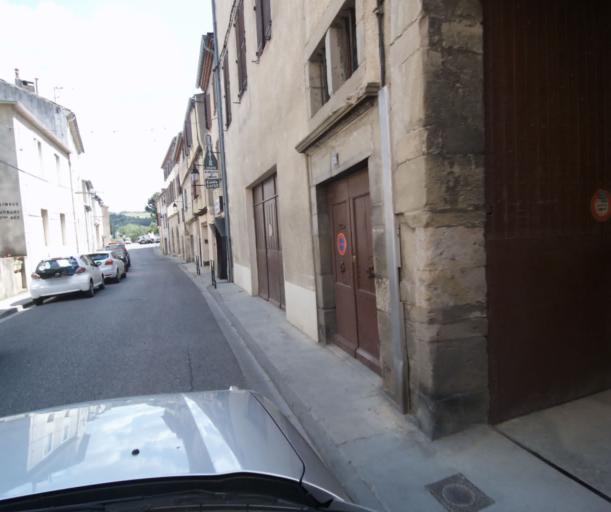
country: FR
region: Languedoc-Roussillon
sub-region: Departement de l'Aude
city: Limoux
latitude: 43.0525
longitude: 2.2215
